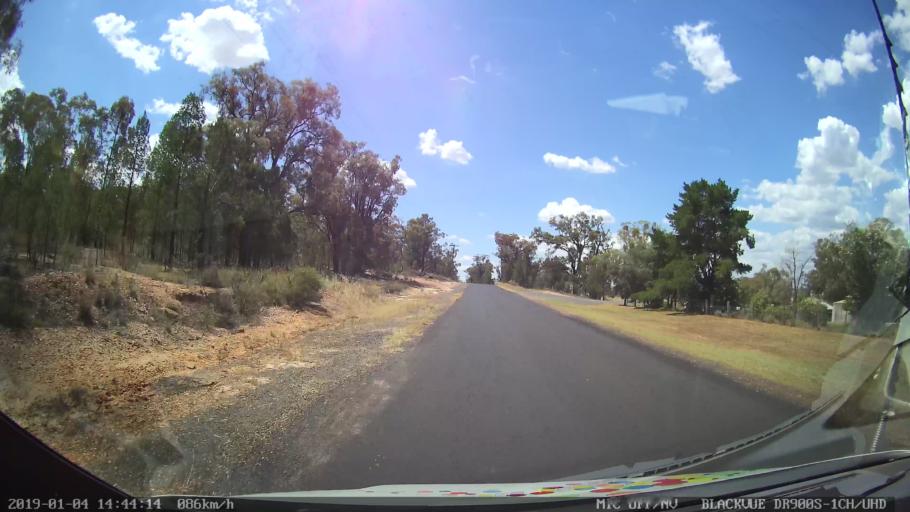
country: AU
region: New South Wales
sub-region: Dubbo Municipality
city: Dubbo
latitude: -32.1087
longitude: 148.6552
